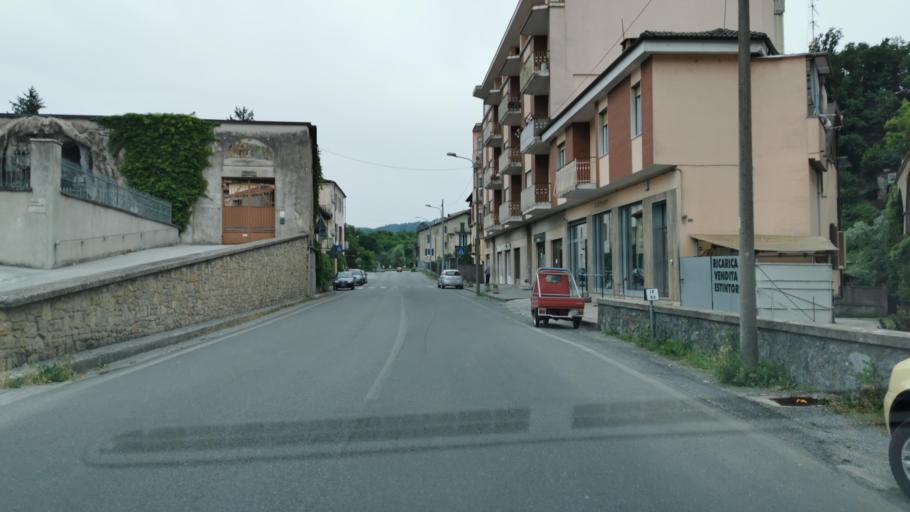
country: IT
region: Piedmont
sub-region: Provincia di Cuneo
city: Ceva
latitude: 44.3850
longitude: 8.0385
